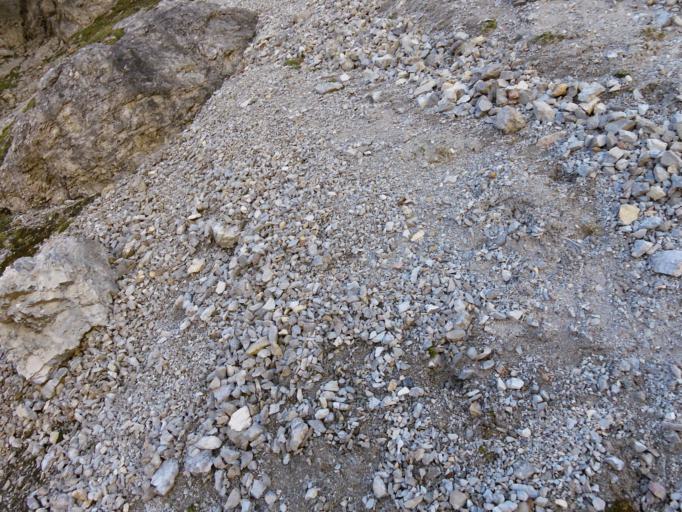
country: AT
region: Tyrol
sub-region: Politischer Bezirk Innsbruck Land
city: Neustift im Stubaital
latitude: 47.1346
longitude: 11.2756
